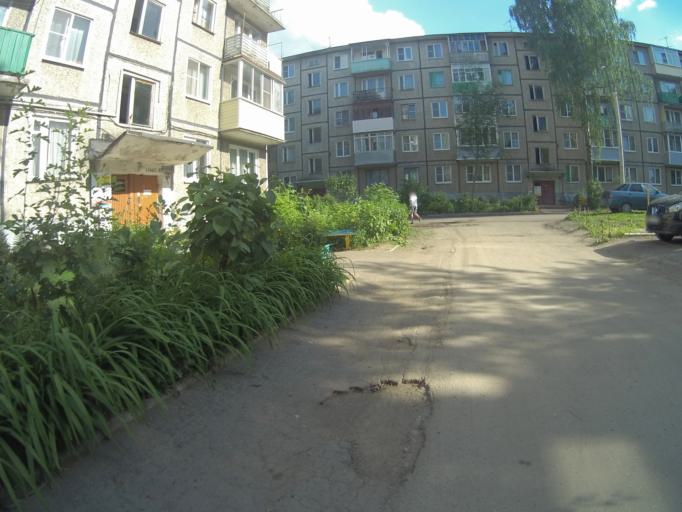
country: RU
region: Vladimir
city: Bogolyubovo
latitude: 56.1737
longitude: 40.4832
